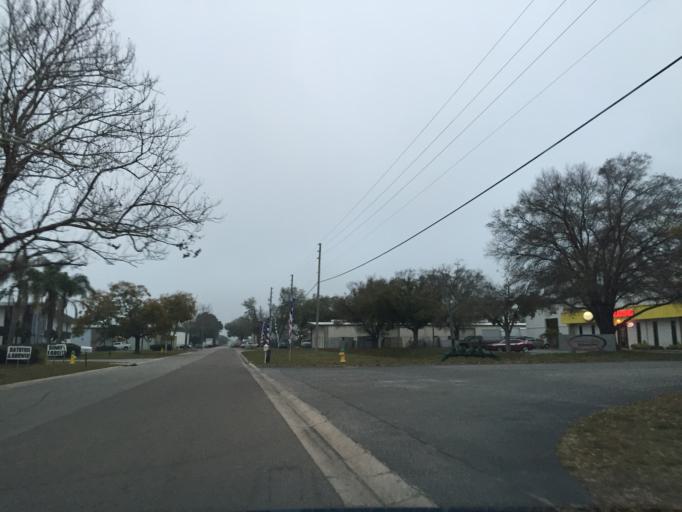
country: US
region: Florida
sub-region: Pinellas County
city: South Highpoint
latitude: 27.8851
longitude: -82.6963
